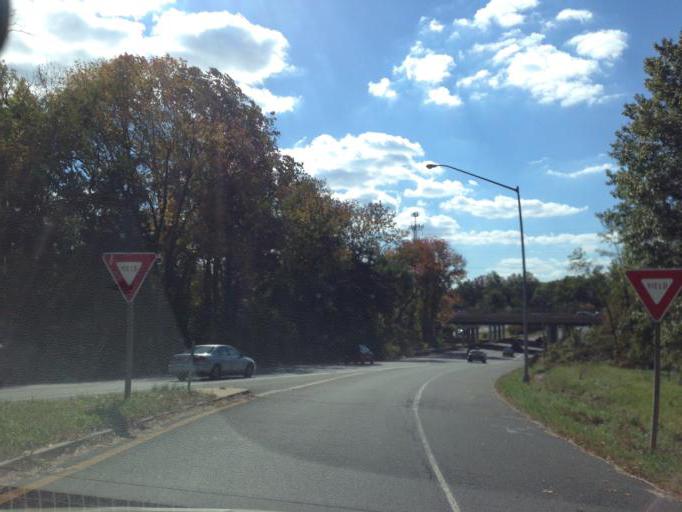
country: US
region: Maryland
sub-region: Howard County
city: Ellicott City
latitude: 39.2789
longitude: -76.8195
